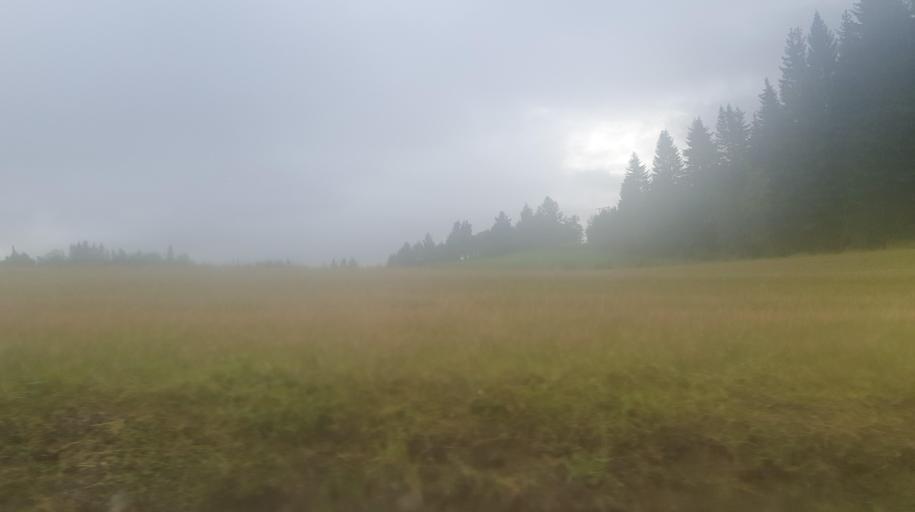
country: NO
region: Nord-Trondelag
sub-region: Levanger
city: Skogn
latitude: 63.6203
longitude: 11.1641
